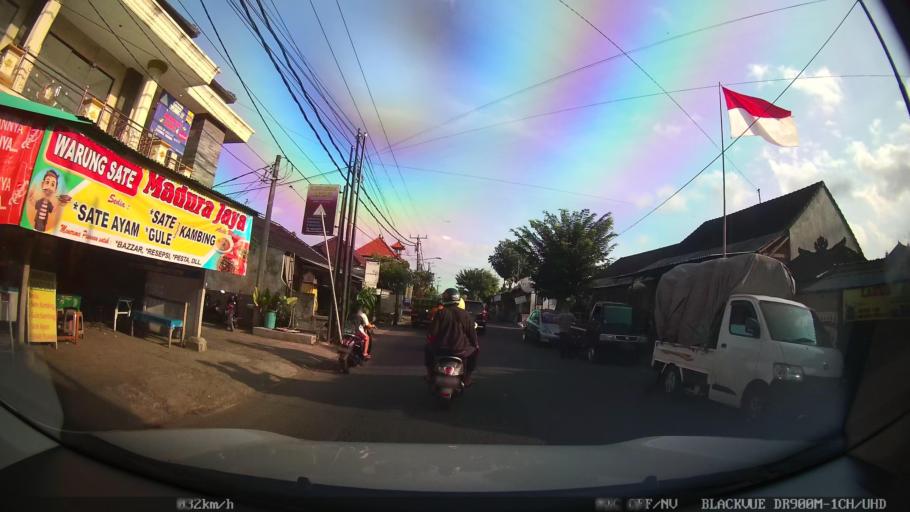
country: ID
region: Bali
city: Banjar Batur
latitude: -8.6086
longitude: 115.2134
